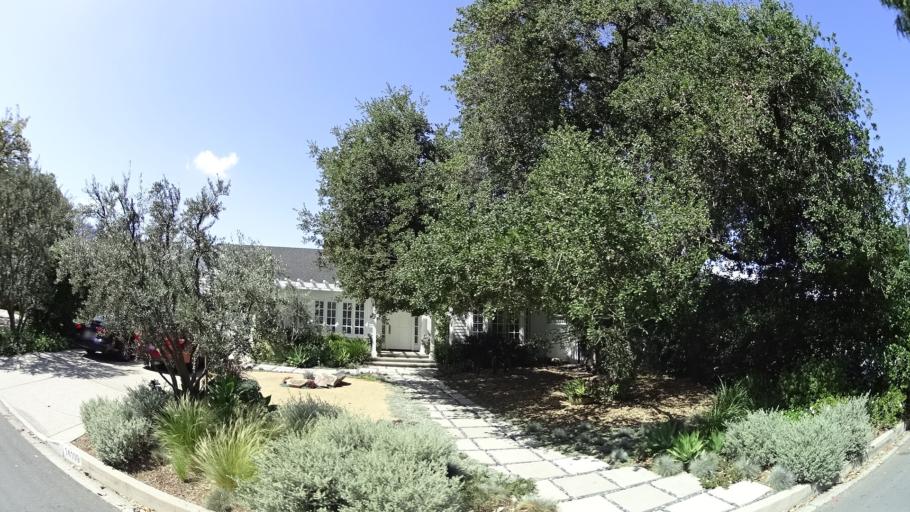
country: US
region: California
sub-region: Los Angeles County
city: Sherman Oaks
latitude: 34.1469
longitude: -118.4403
